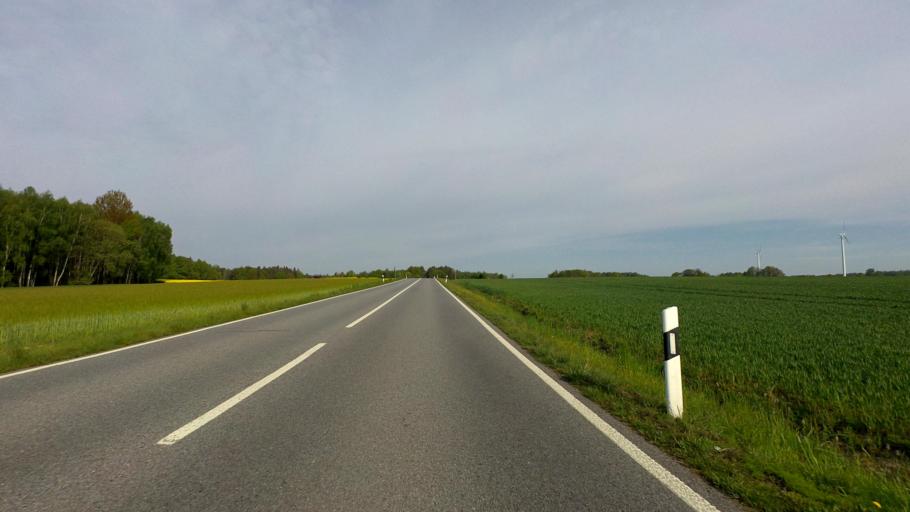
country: DE
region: Saxony
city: Stolpen
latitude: 51.0666
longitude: 14.0511
